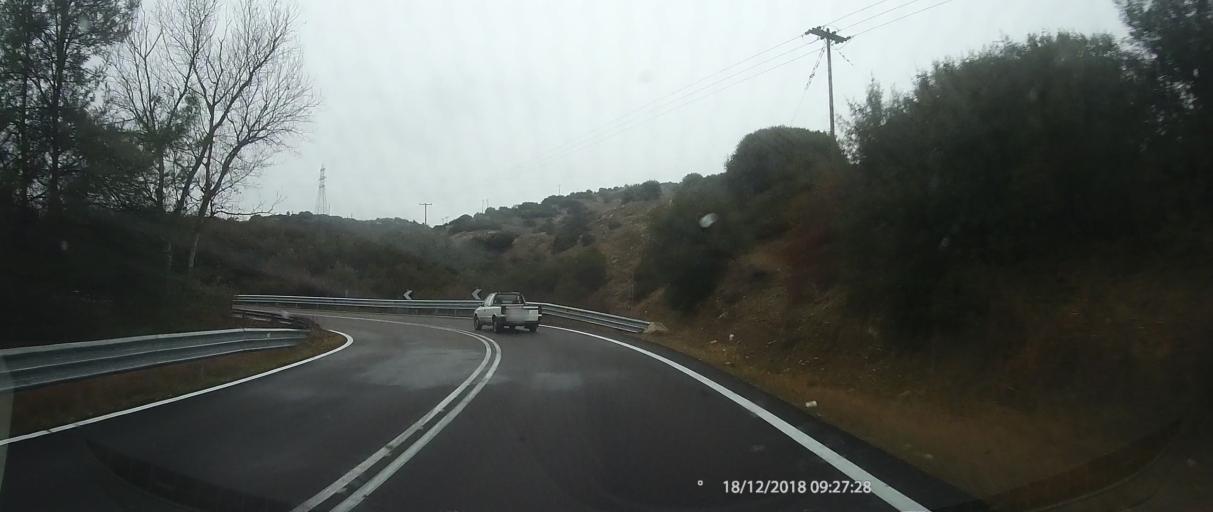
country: GR
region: Thessaly
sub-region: Nomos Larisis
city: Elassona
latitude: 39.9182
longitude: 22.1770
